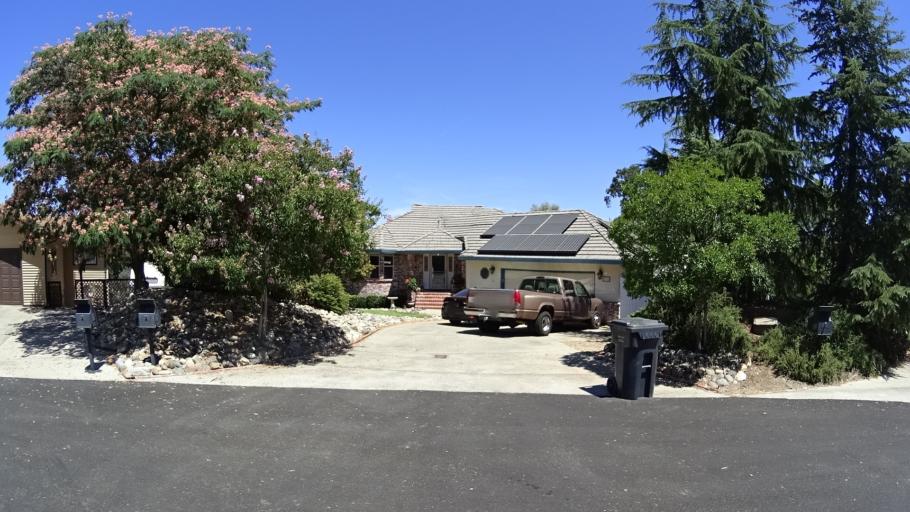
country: US
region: California
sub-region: Calaveras County
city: Valley Springs
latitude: 38.1623
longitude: -120.8223
